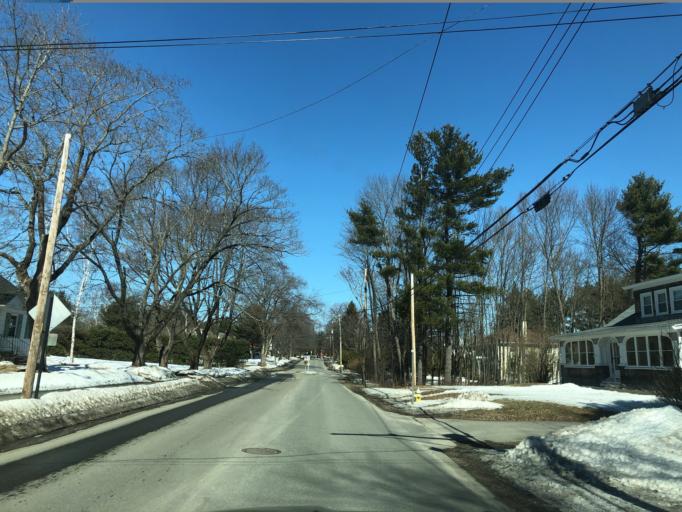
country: US
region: Maine
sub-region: Penobscot County
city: Brewer
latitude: 44.8132
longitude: -68.7530
